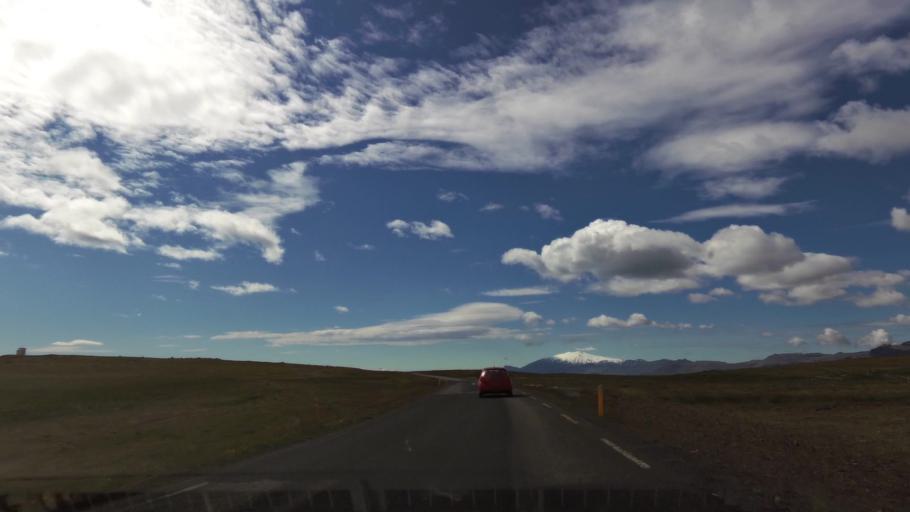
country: IS
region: West
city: Stykkisholmur
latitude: 64.8089
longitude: -23.0905
